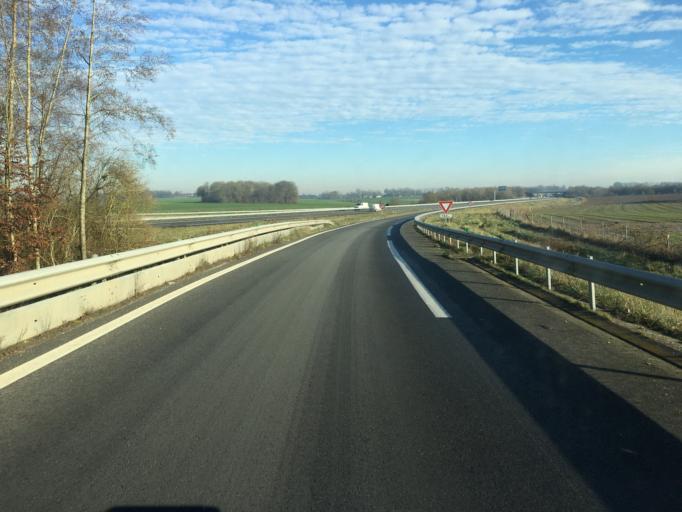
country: FR
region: Haute-Normandie
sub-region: Departement de la Seine-Maritime
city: Yerville
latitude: 49.6516
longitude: 0.8467
